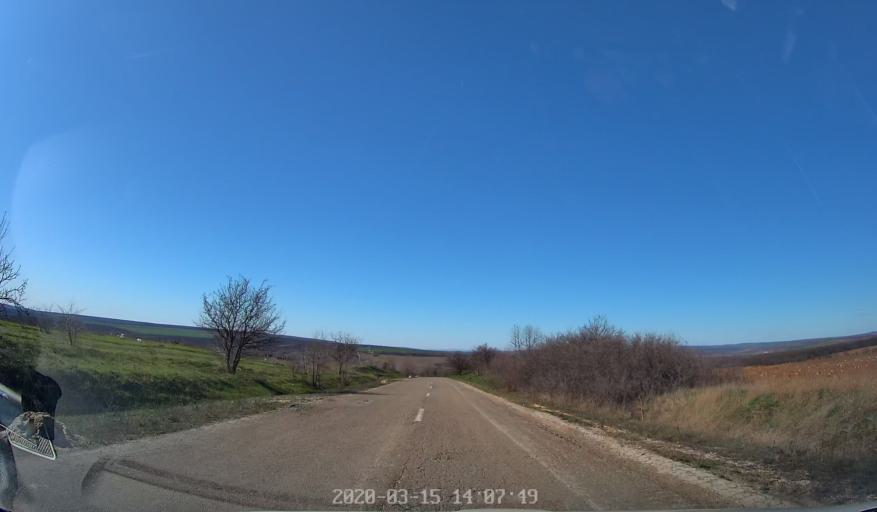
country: MD
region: Orhei
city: Orhei
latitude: 47.3050
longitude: 28.9444
